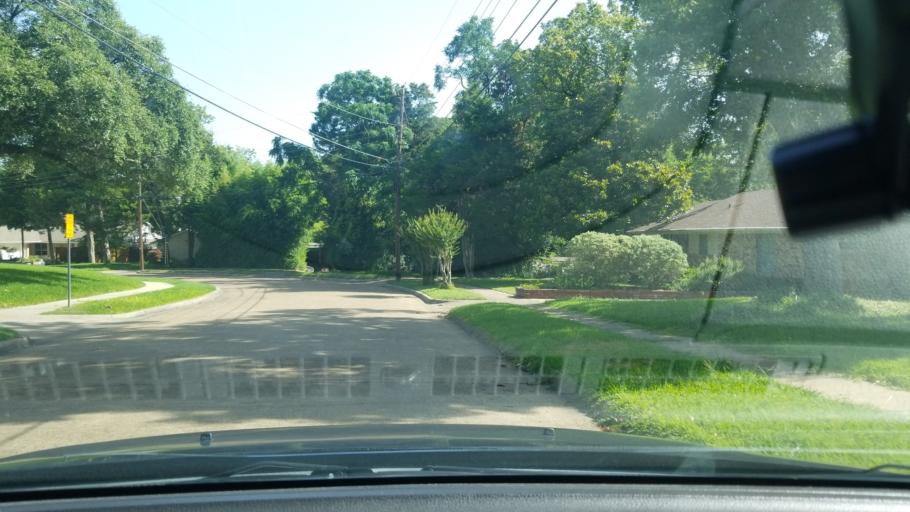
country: US
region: Texas
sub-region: Dallas County
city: Mesquite
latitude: 32.8118
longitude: -96.6909
